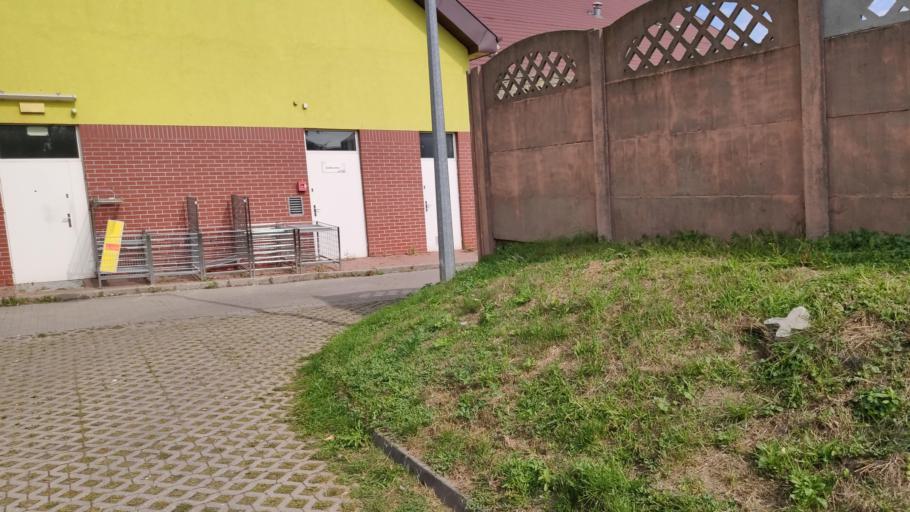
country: PL
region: Kujawsko-Pomorskie
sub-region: Powiat zninski
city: Znin
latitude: 52.8489
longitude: 17.7185
